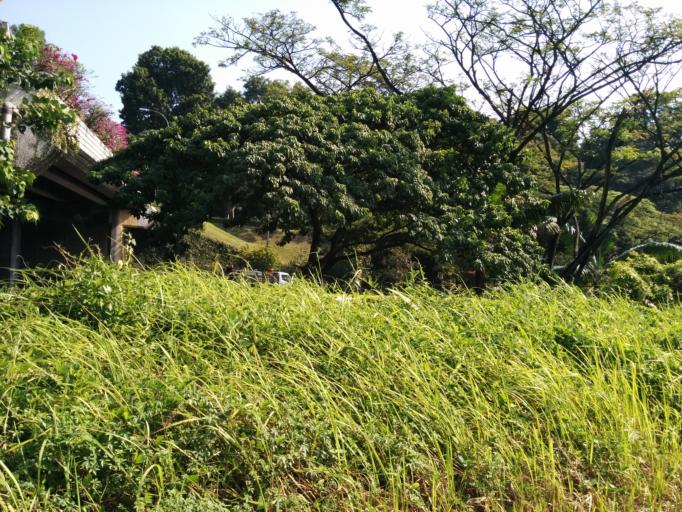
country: SG
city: Singapore
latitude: 1.2845
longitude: 103.8014
